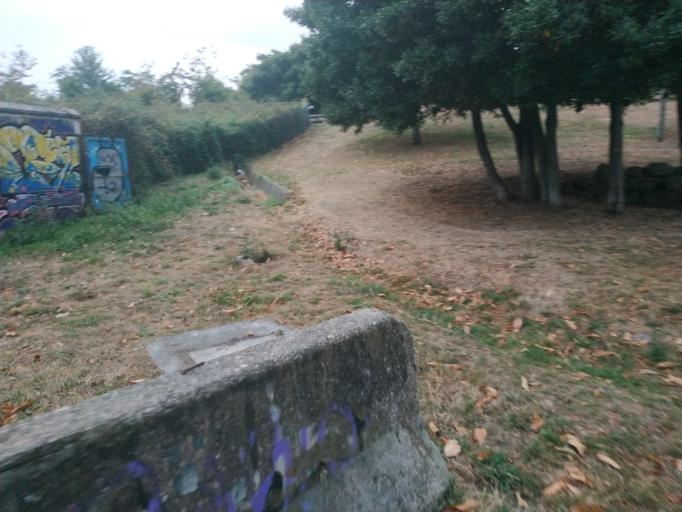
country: ES
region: Galicia
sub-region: Provincia da Coruna
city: A Coruna
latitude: 43.3468
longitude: -8.3946
